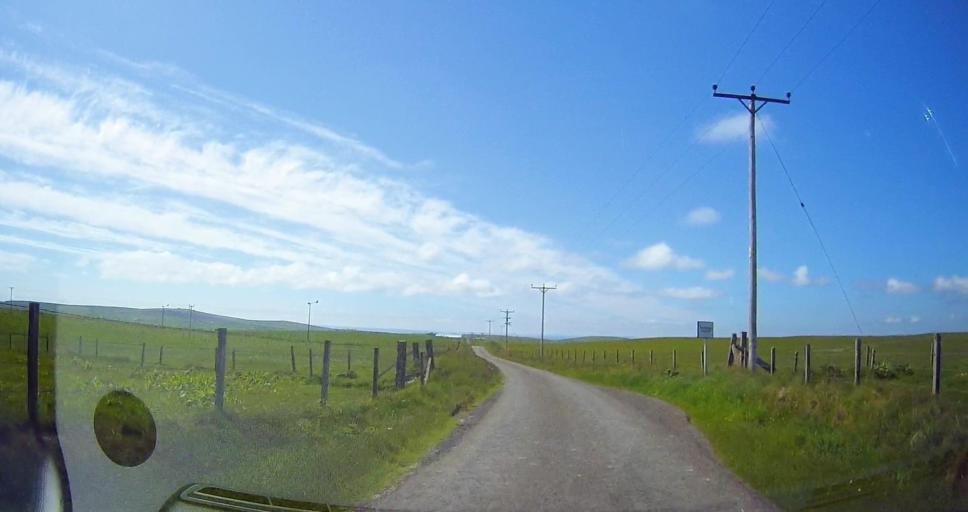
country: GB
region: Scotland
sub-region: Orkney Islands
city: Kirkwall
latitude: 58.8125
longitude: -2.9248
